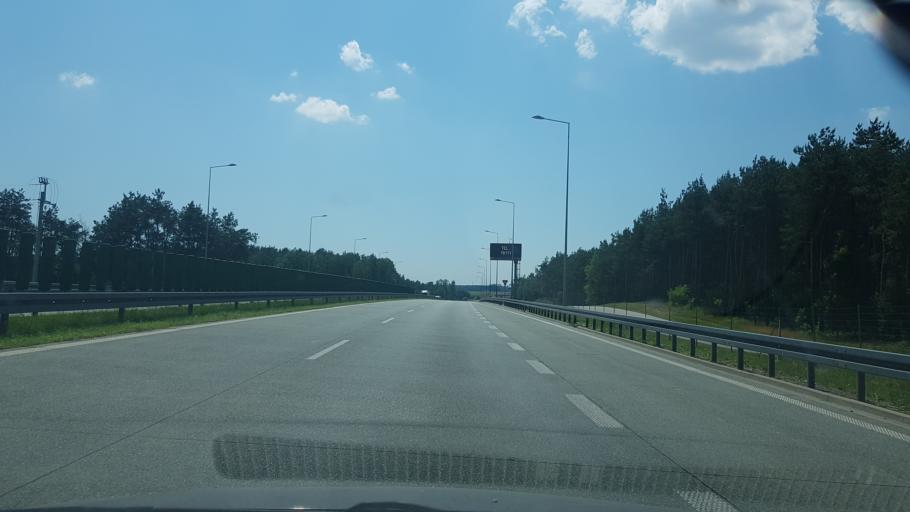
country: PL
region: Lodz Voivodeship
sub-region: Powiat rawski
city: Rawa Mazowiecka
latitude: 51.7022
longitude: 20.2193
